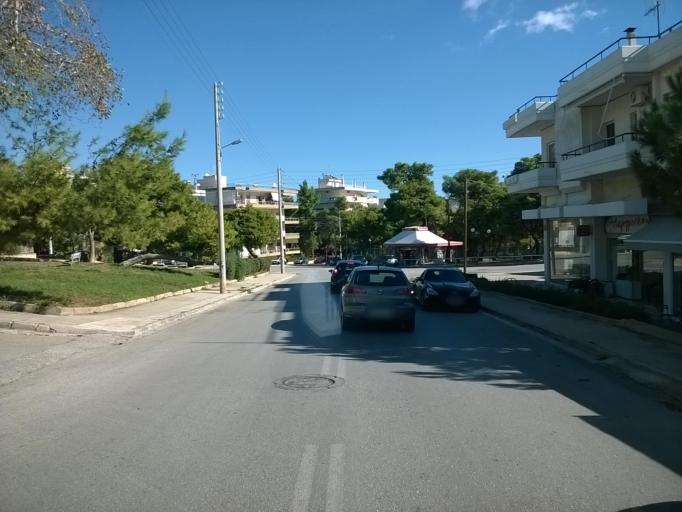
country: GR
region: Attica
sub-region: Nomarchia Anatolikis Attikis
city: Vouliagmeni
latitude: 37.8171
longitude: 23.7960
